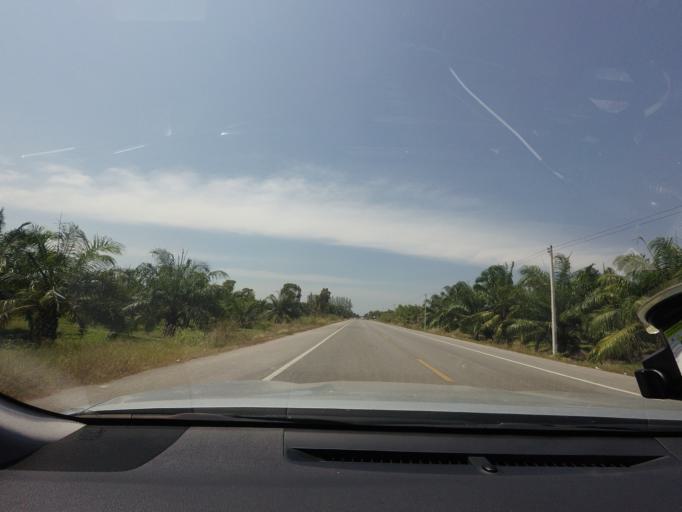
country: TH
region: Surat Thani
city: Tha Chang
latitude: 9.2166
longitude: 99.2077
